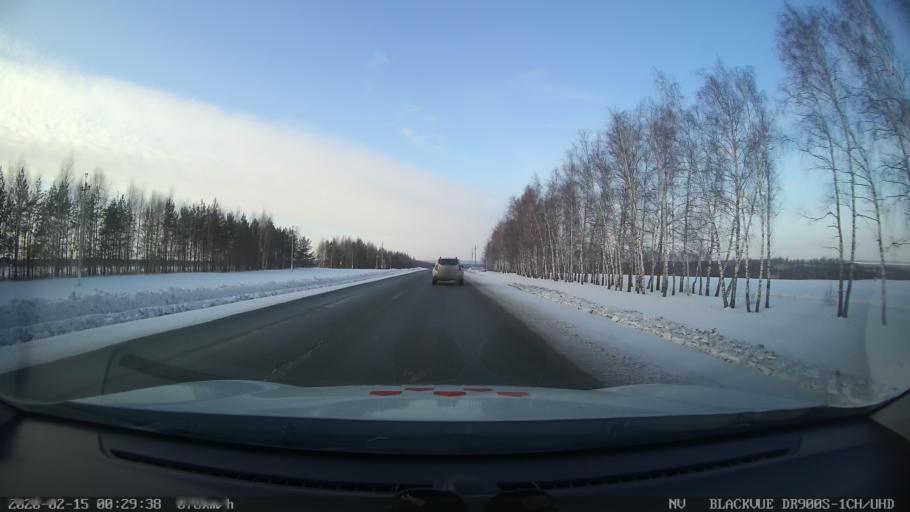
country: RU
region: Tatarstan
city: Verkhniy Uslon
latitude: 55.6526
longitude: 48.8660
